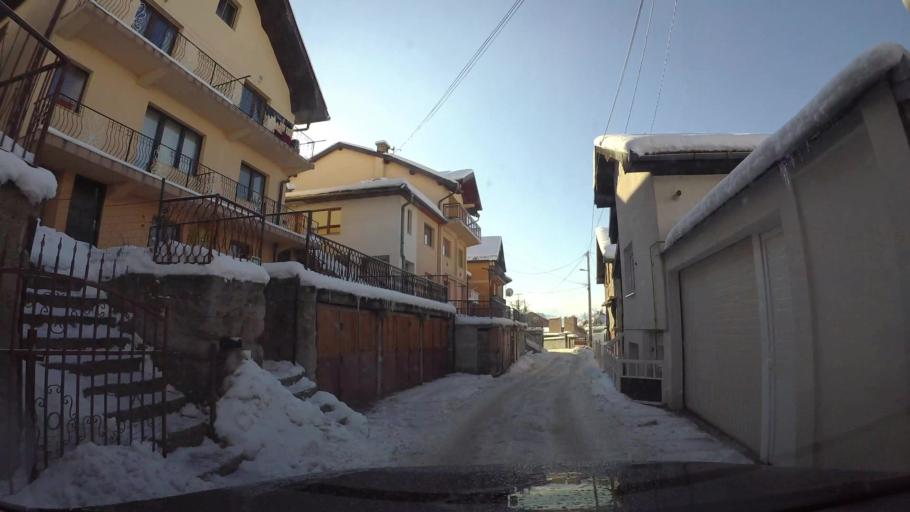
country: BA
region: Federation of Bosnia and Herzegovina
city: Kobilja Glava
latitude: 43.8763
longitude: 18.4224
